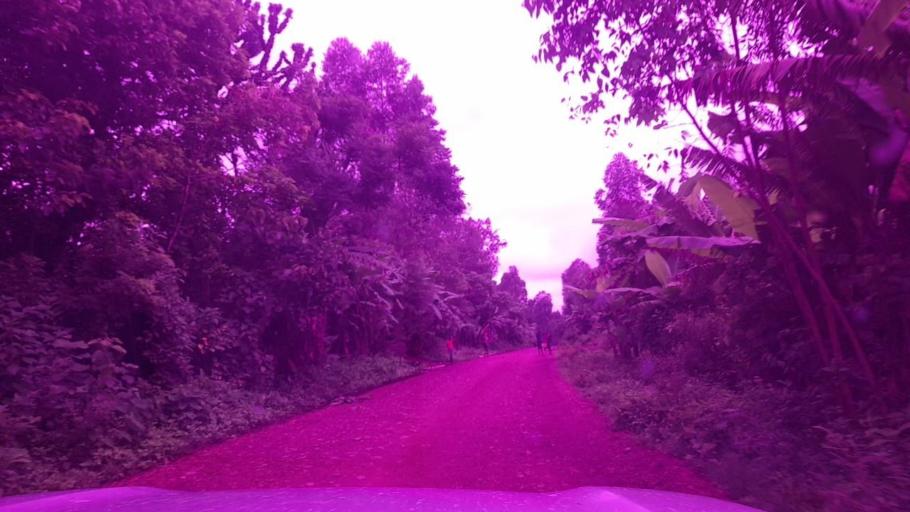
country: ET
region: Southern Nations, Nationalities, and People's Region
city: Bonga
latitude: 7.5739
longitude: 36.0265
